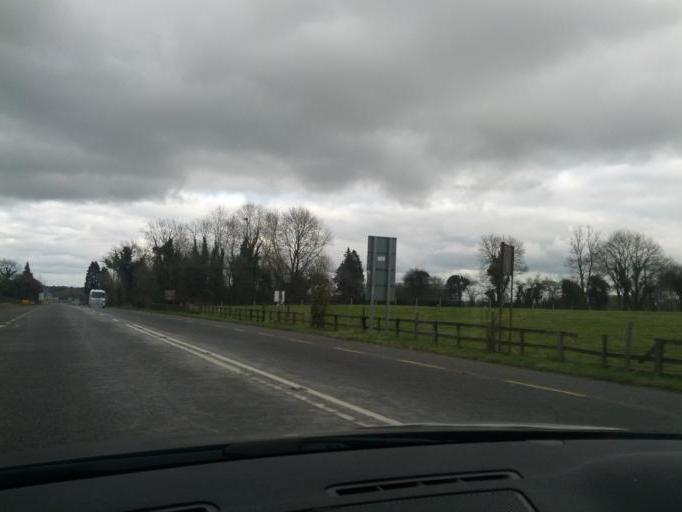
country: IE
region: Leinster
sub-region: An Iarmhi
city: Moate
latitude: 53.3957
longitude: -7.6962
